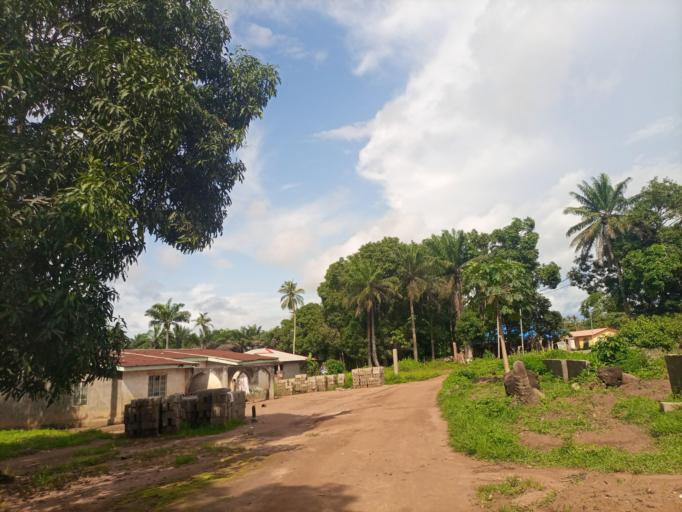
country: SL
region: Northern Province
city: Masoyila
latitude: 8.6271
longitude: -13.1775
